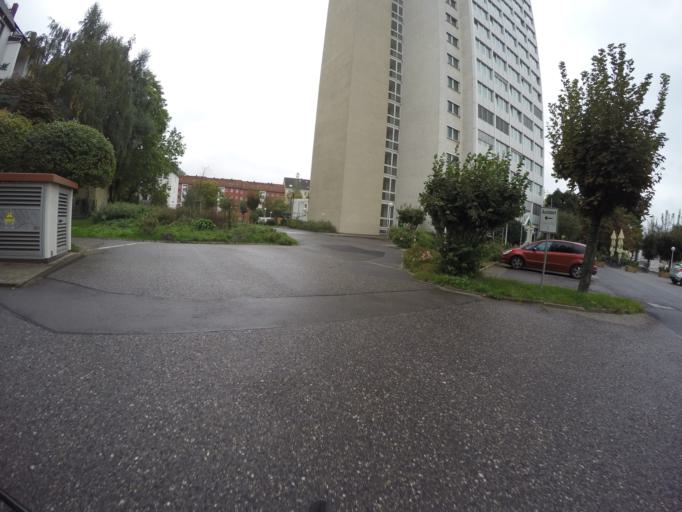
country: DE
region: Saxony
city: Chemnitz
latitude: 50.8246
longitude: 12.9271
